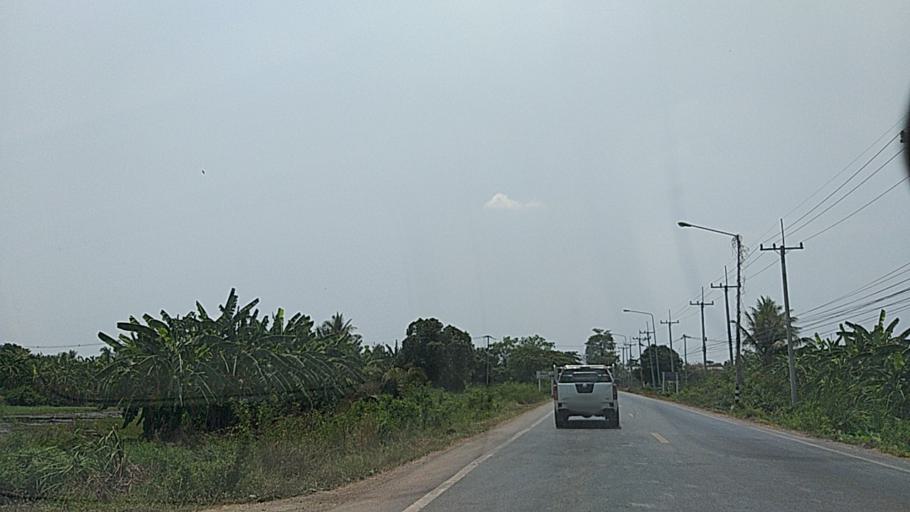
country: TH
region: Chachoengsao
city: Bang Nam Priao
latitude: 13.8689
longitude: 100.9670
